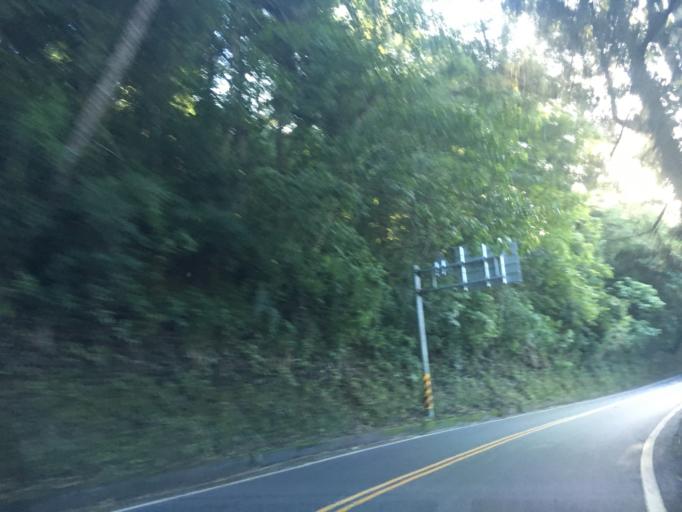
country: TW
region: Taiwan
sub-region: Nantou
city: Puli
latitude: 24.0246
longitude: 121.1347
